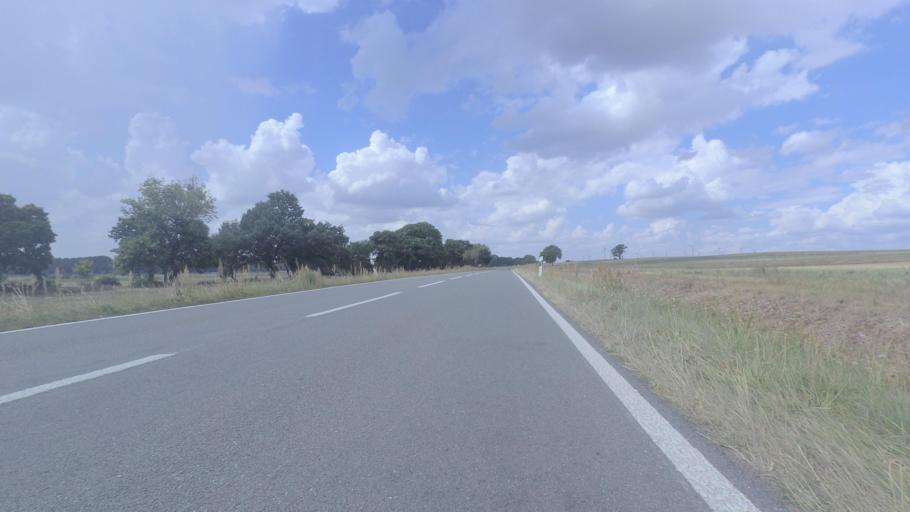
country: DE
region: Brandenburg
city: Wittstock
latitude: 53.1962
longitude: 12.4615
